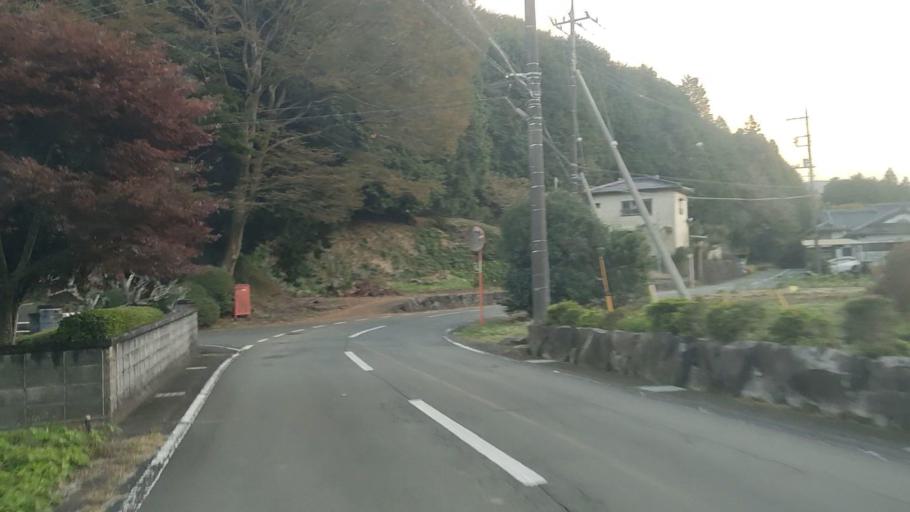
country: JP
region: Kanagawa
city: Yugawara
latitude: 35.1244
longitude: 139.0154
